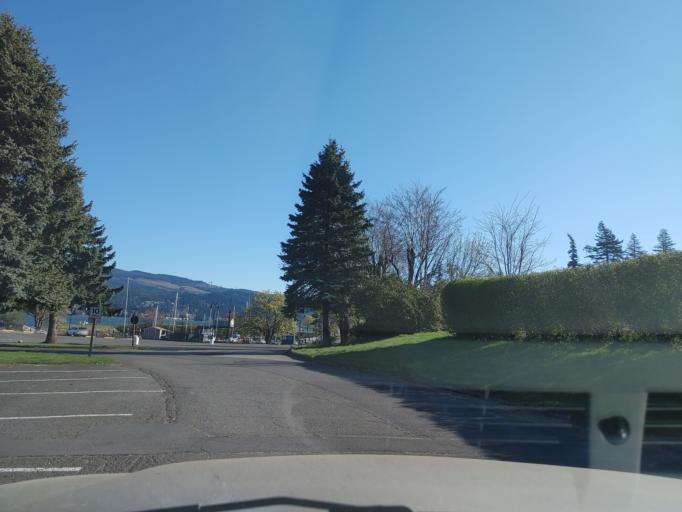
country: US
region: Oregon
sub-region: Hood River County
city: Cascade Locks
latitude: 45.6704
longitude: -121.8928
